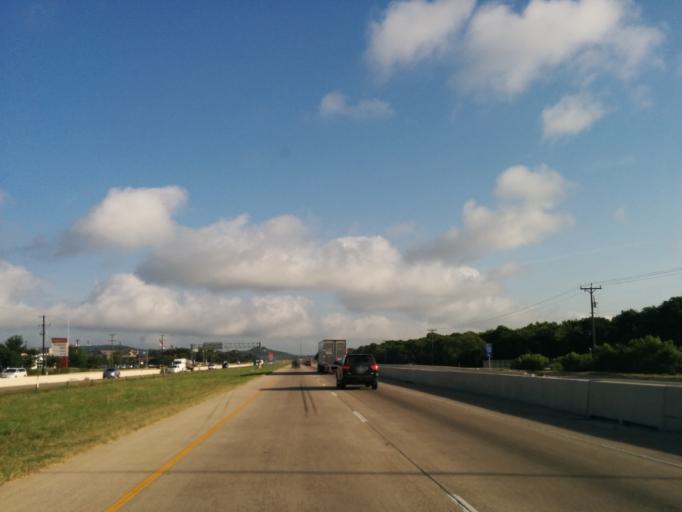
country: US
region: Texas
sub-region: Bexar County
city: Cross Mountain
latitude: 29.6380
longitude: -98.6153
